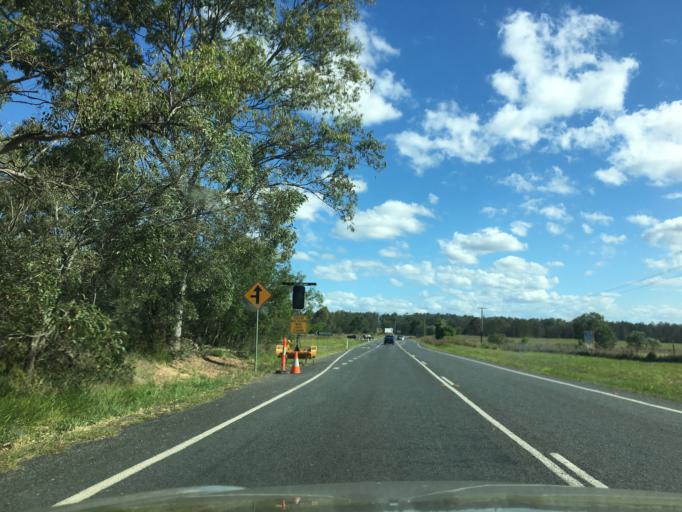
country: AU
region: Queensland
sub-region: Logan
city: Logan Reserve
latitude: -27.7480
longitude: 153.1258
